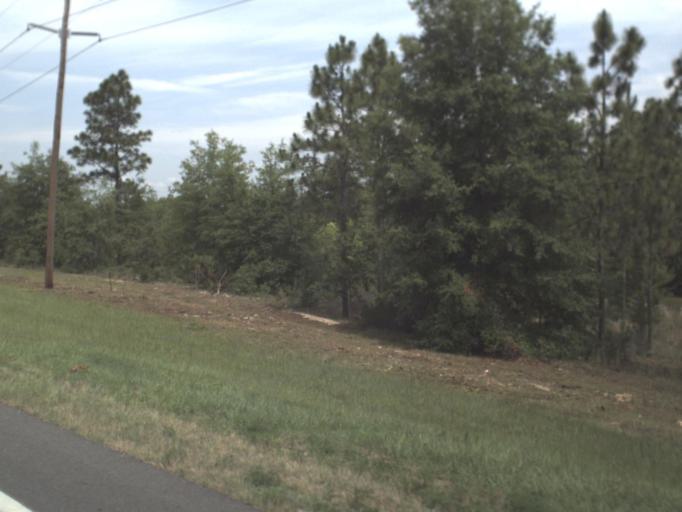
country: US
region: Florida
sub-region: Putnam County
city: Interlachen
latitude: 29.6238
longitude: -81.9184
